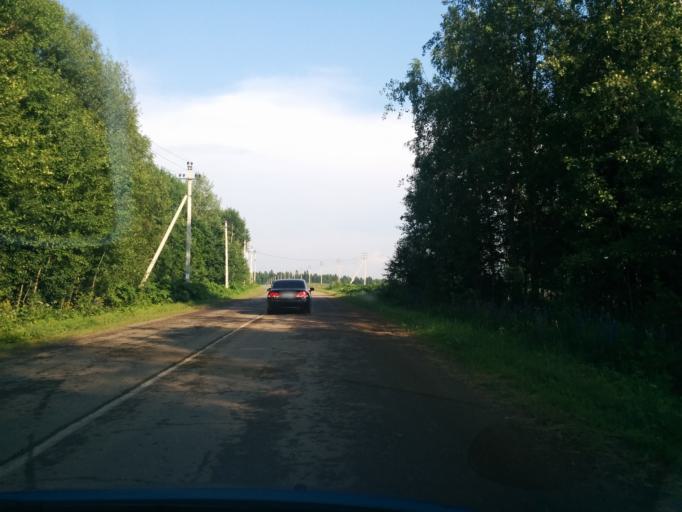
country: RU
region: Perm
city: Polazna
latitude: 58.2411
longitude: 56.2690
